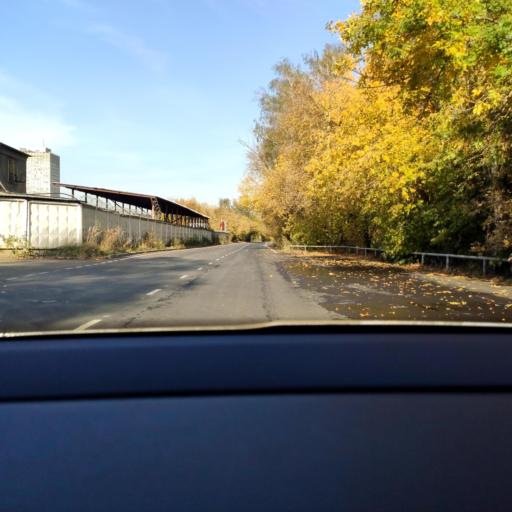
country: RU
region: Moscow
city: Sokol'niki
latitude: 55.8048
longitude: 37.6557
